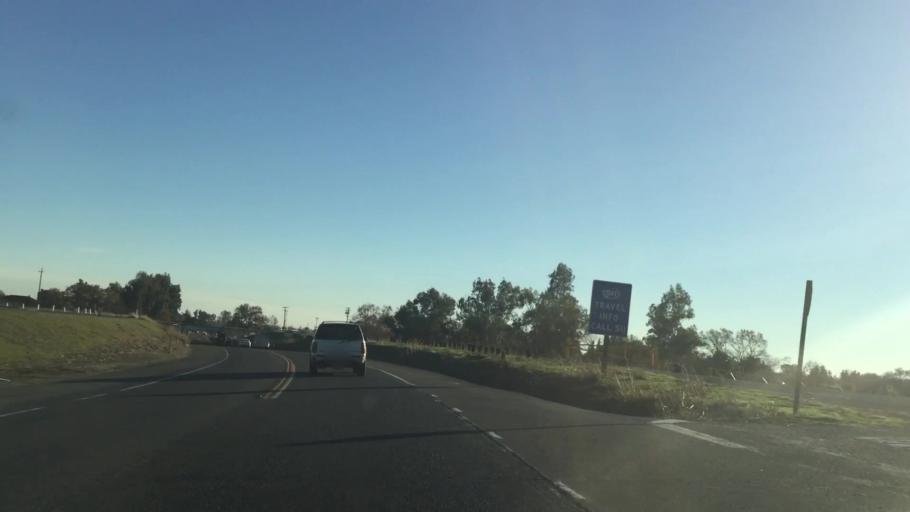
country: US
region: California
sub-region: Yuba County
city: Marysville
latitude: 39.1615
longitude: -121.5909
